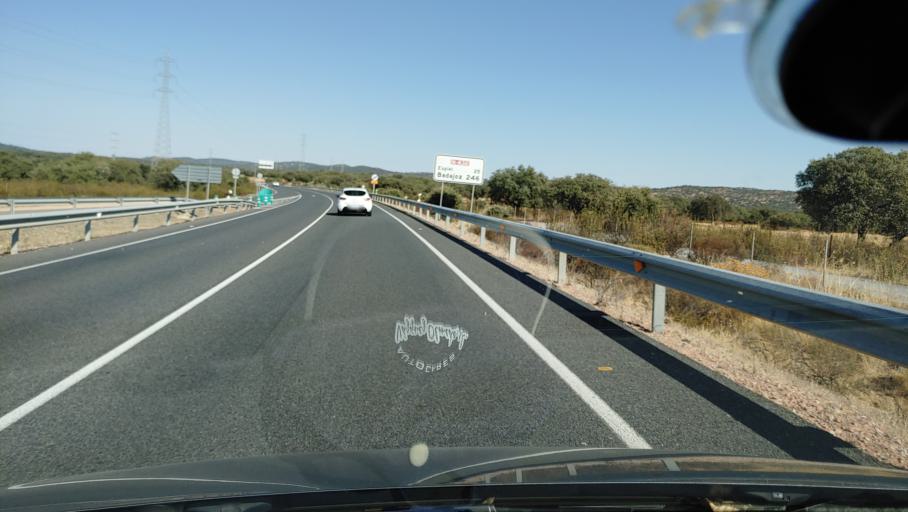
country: ES
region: Andalusia
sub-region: Province of Cordoba
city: Obejo
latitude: 38.0536
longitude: -4.8112
